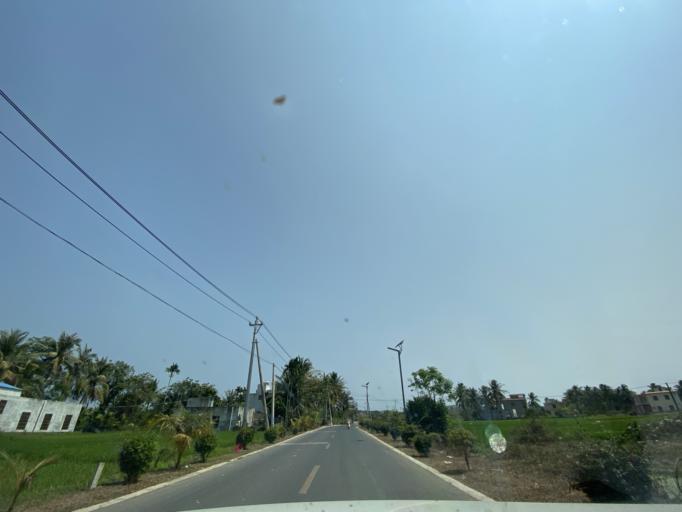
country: CN
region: Hainan
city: Yingzhou
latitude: 18.4188
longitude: 109.8134
